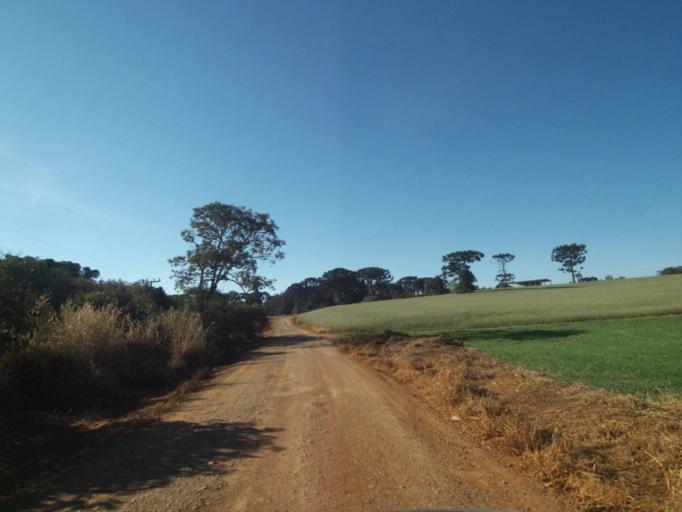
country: BR
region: Parana
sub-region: Tibagi
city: Tibagi
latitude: -24.5374
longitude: -50.4970
